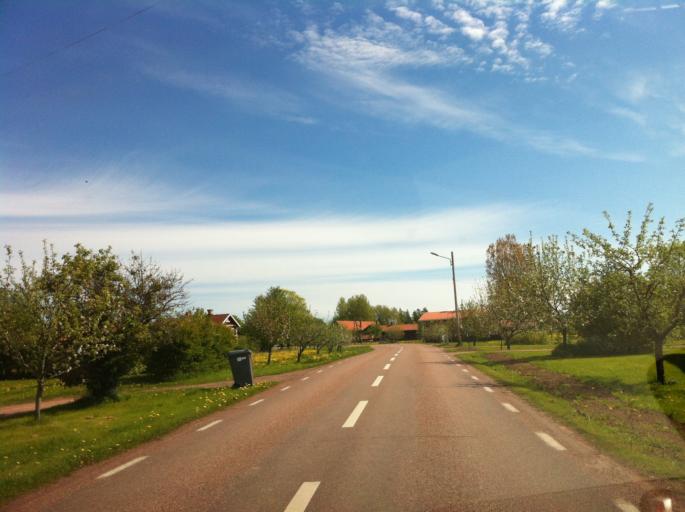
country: SE
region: Dalarna
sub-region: Mora Kommun
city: Mora
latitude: 60.9079
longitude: 14.6116
